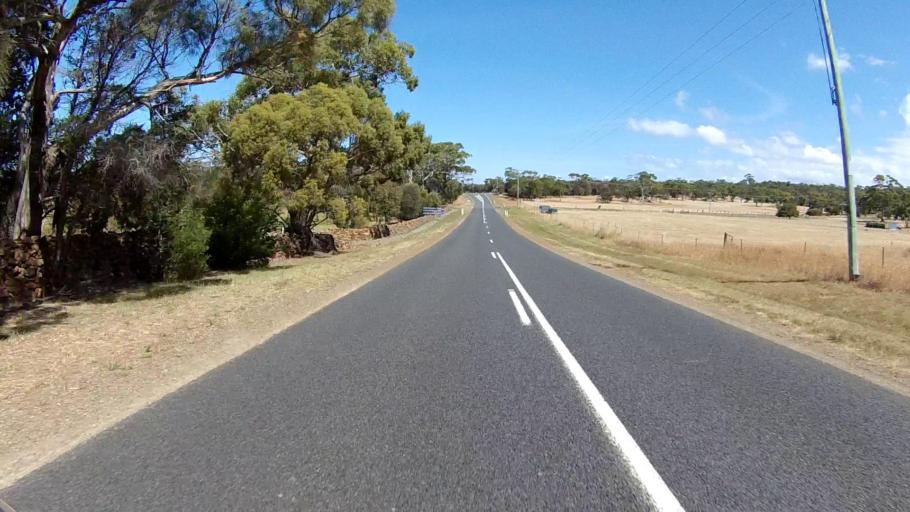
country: AU
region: Tasmania
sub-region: Sorell
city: Sorell
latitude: -42.1404
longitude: 148.0701
